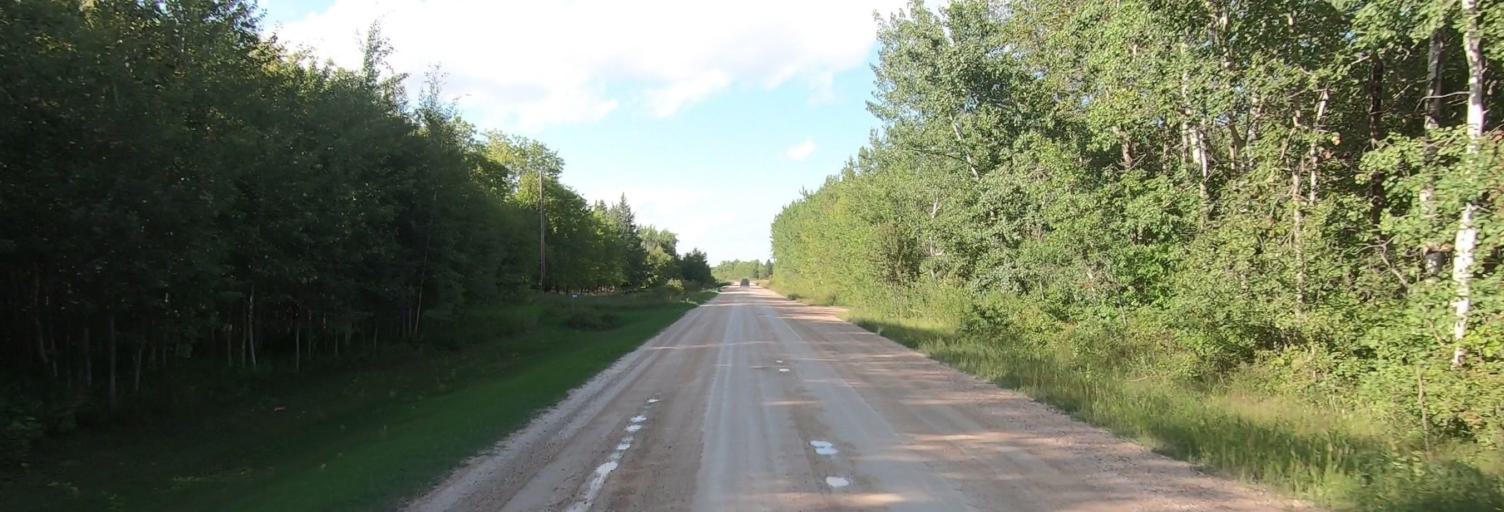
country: CA
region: Manitoba
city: Selkirk
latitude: 50.2399
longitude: -96.8440
